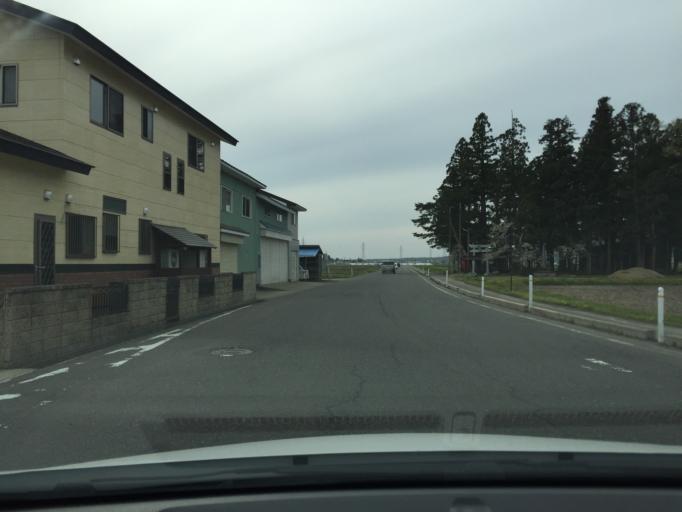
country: JP
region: Fukushima
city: Inawashiro
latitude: 37.5483
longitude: 140.1255
